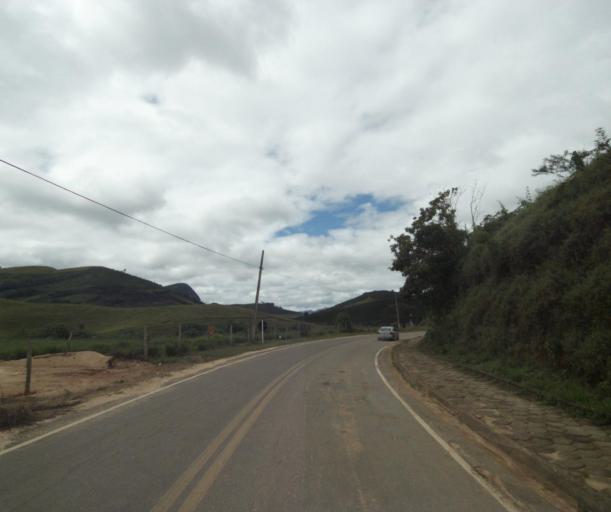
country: BR
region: Espirito Santo
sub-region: Irupi
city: Irupi
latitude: -20.3514
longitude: -41.6328
